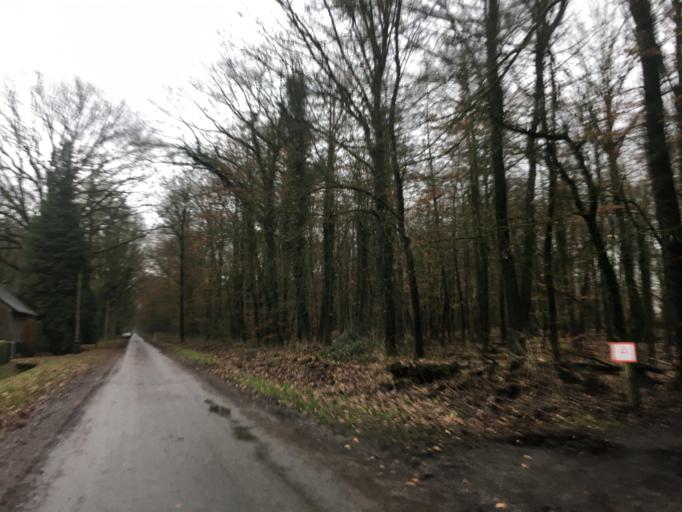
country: DE
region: North Rhine-Westphalia
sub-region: Regierungsbezirk Munster
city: Dulmen
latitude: 51.7477
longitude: 7.3015
